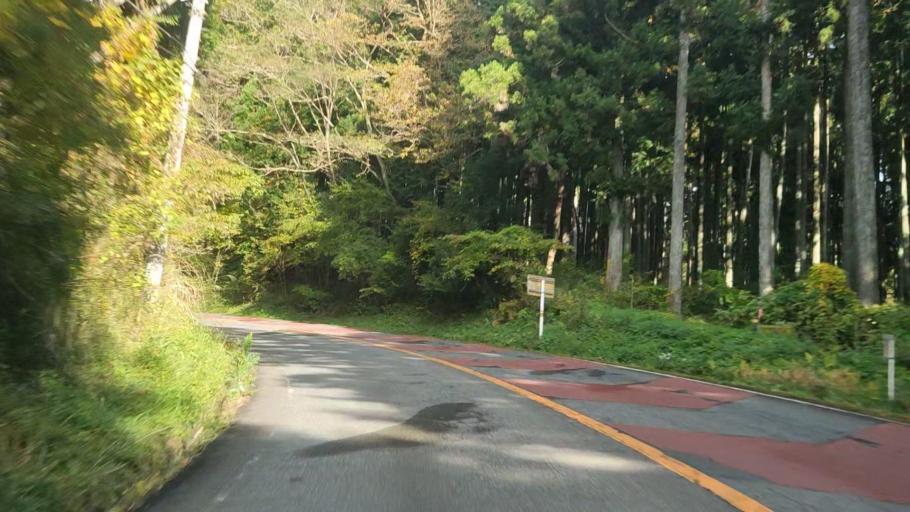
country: JP
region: Shizuoka
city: Fujinomiya
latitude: 35.2909
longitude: 138.6643
